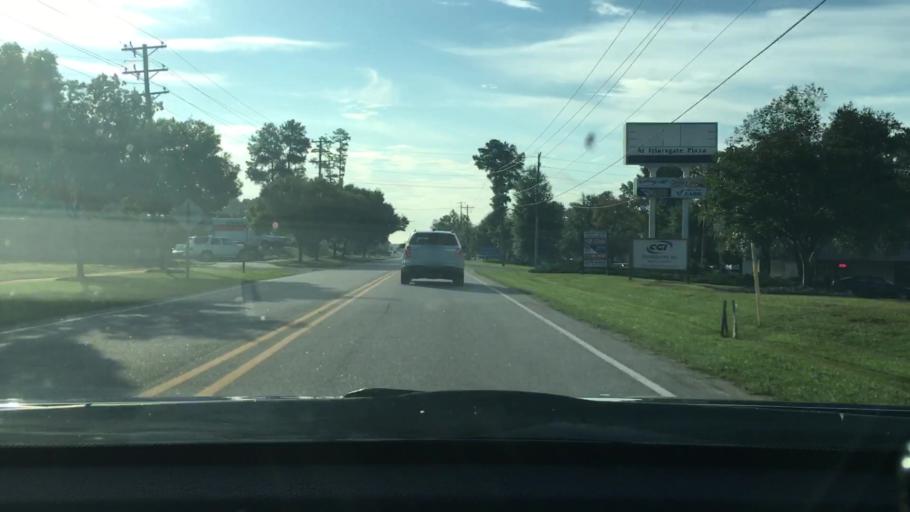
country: US
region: South Carolina
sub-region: Lexington County
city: Irmo
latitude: 34.1068
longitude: -81.1889
